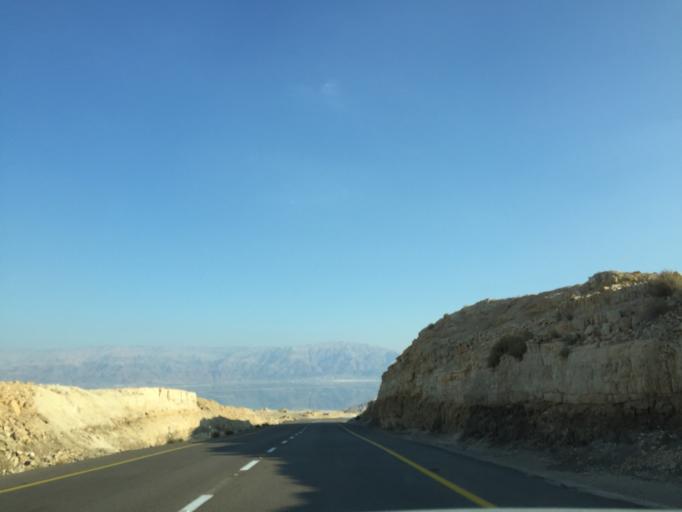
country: IL
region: Southern District
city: `En Boqeq
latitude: 31.1589
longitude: 35.3318
